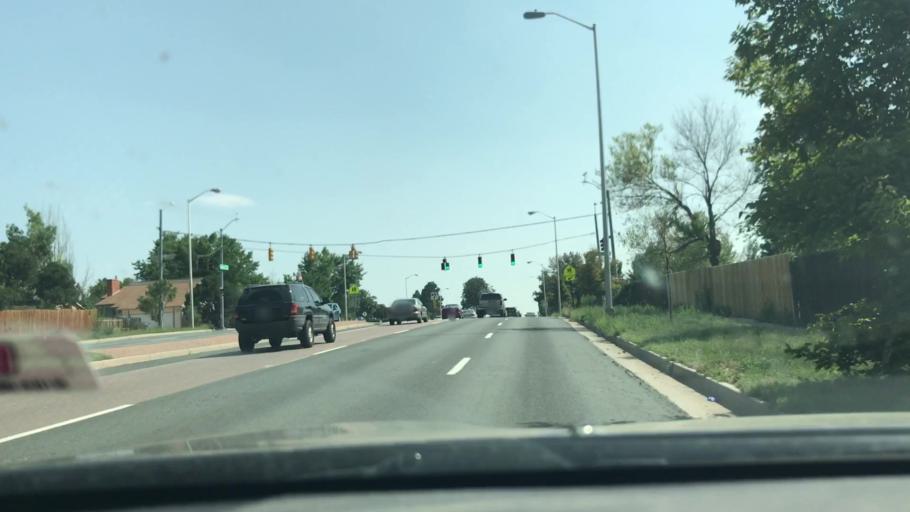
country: US
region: Colorado
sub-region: El Paso County
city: Cimarron Hills
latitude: 38.9223
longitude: -104.7754
